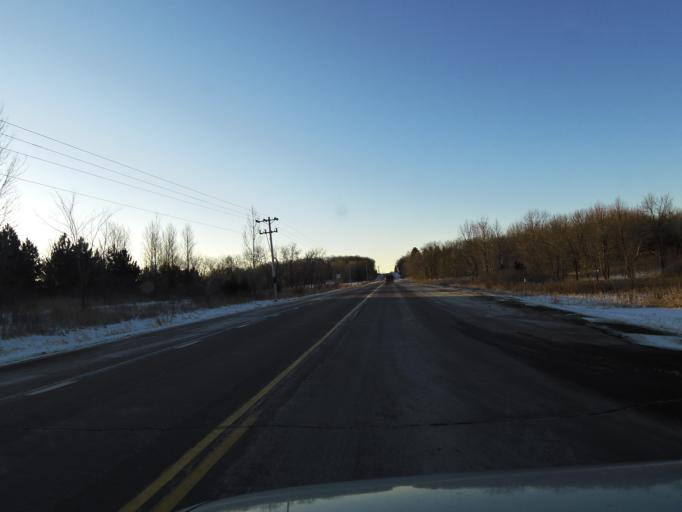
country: US
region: Minnesota
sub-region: Scott County
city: Prior Lake
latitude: 44.6866
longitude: -93.3793
